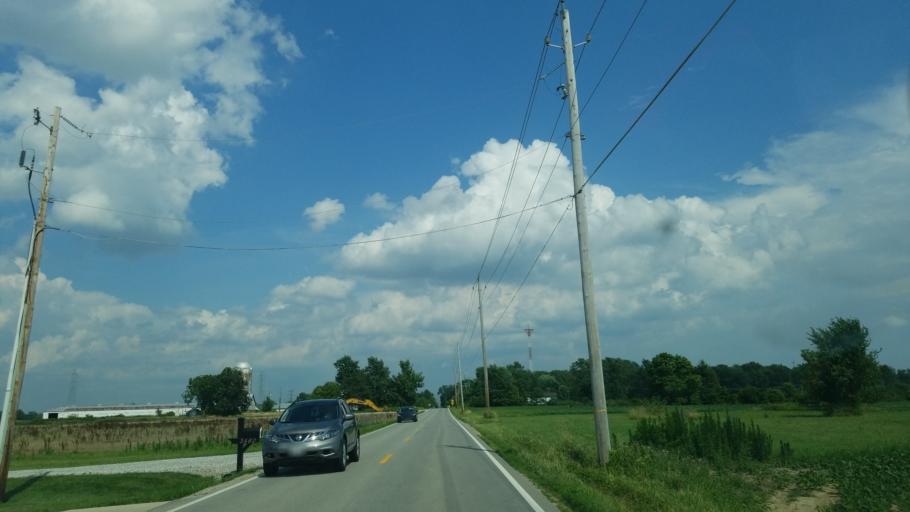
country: US
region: Ohio
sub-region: Delaware County
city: Powell
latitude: 40.2167
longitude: -83.1032
